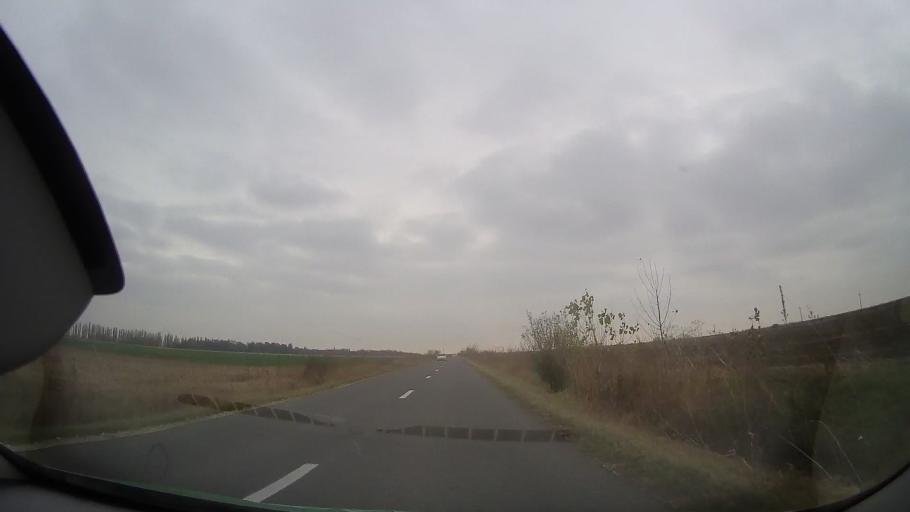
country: RO
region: Ialomita
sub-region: Comuna Alexeni
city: Alexeni
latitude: 44.7409
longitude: 26.7095
